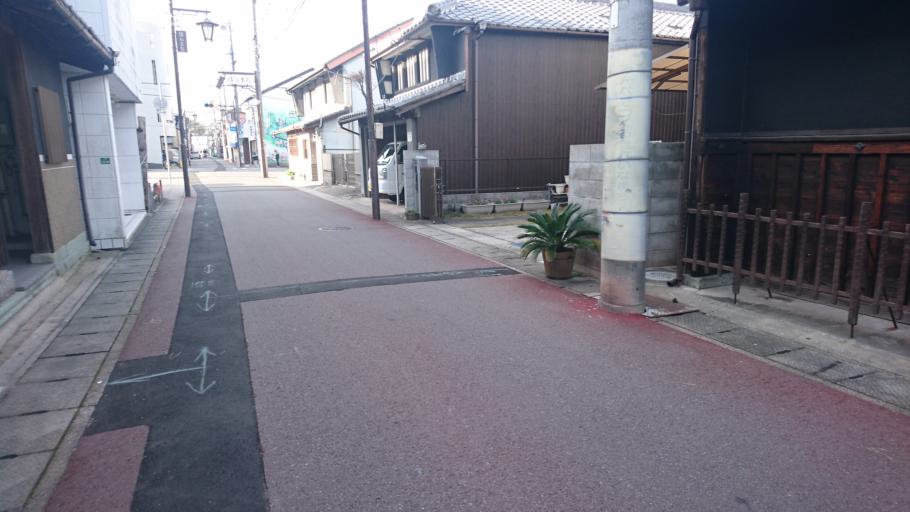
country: JP
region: Hyogo
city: Sandacho
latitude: 34.8847
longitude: 135.2260
